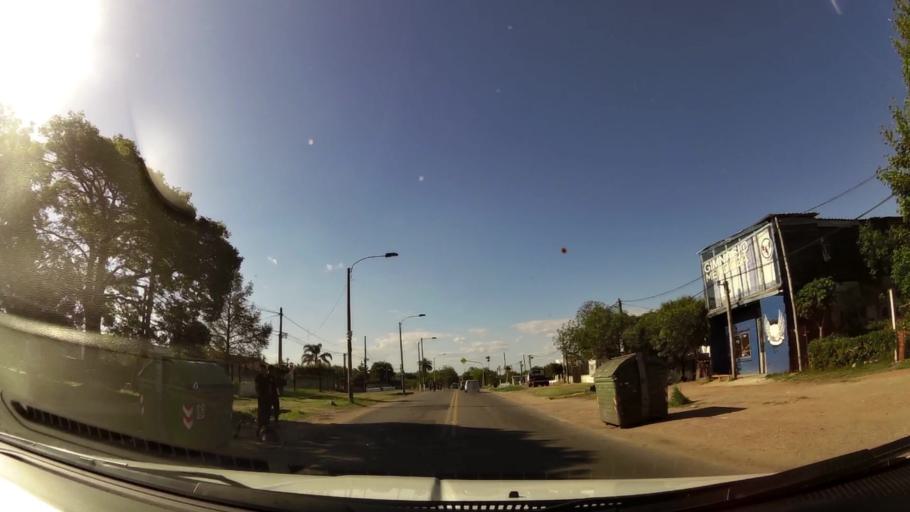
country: UY
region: Canelones
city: La Paz
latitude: -34.8173
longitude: -56.1574
